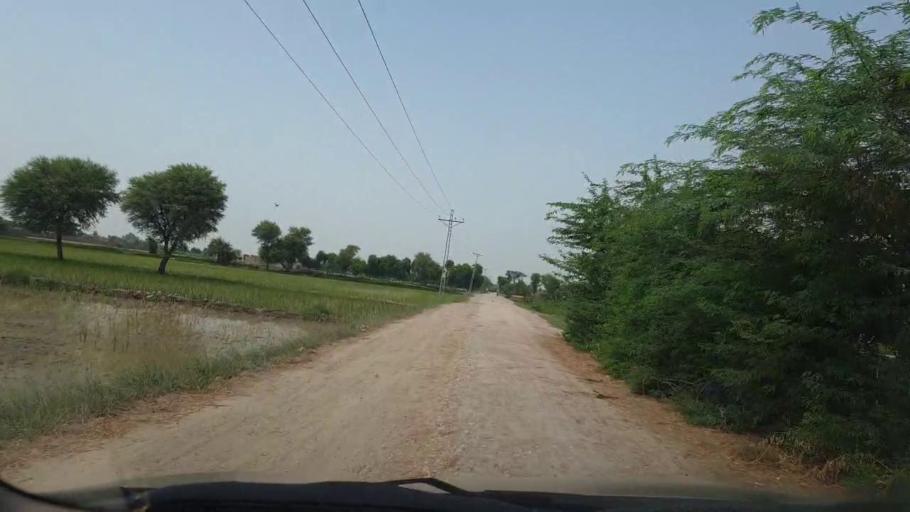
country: PK
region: Sindh
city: Larkana
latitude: 27.5811
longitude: 68.1434
